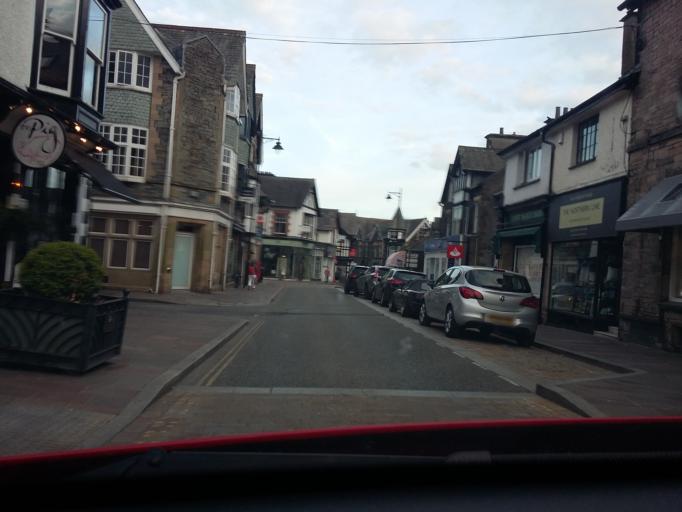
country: GB
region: England
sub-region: Cumbria
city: Windermere
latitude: 54.3788
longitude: -2.9057
